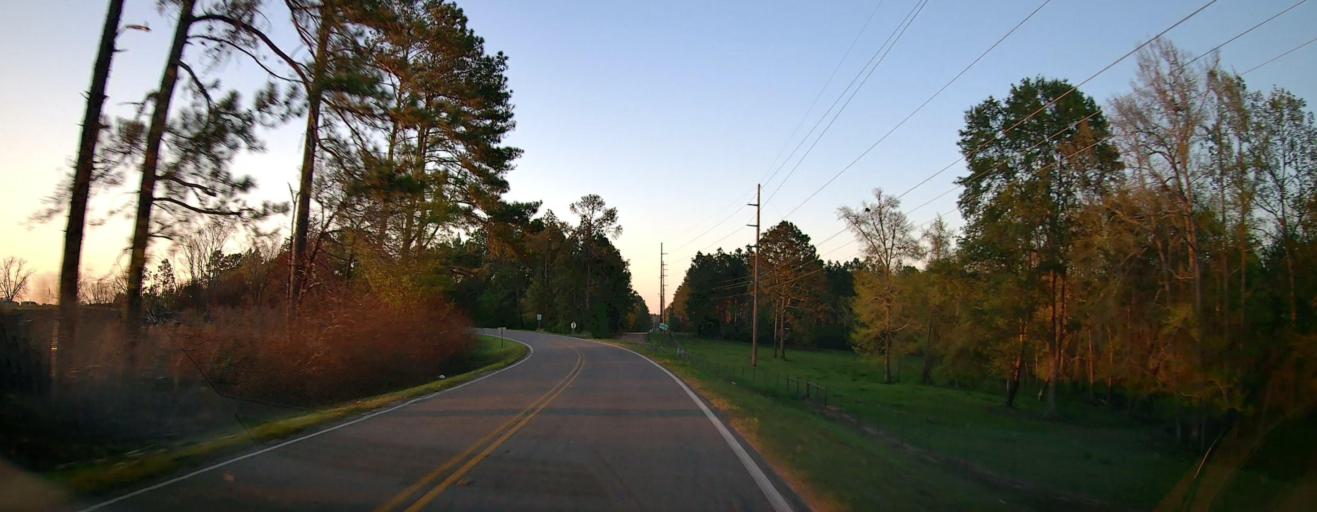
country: US
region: Georgia
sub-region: Ben Hill County
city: Fitzgerald
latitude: 31.7681
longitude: -83.3548
